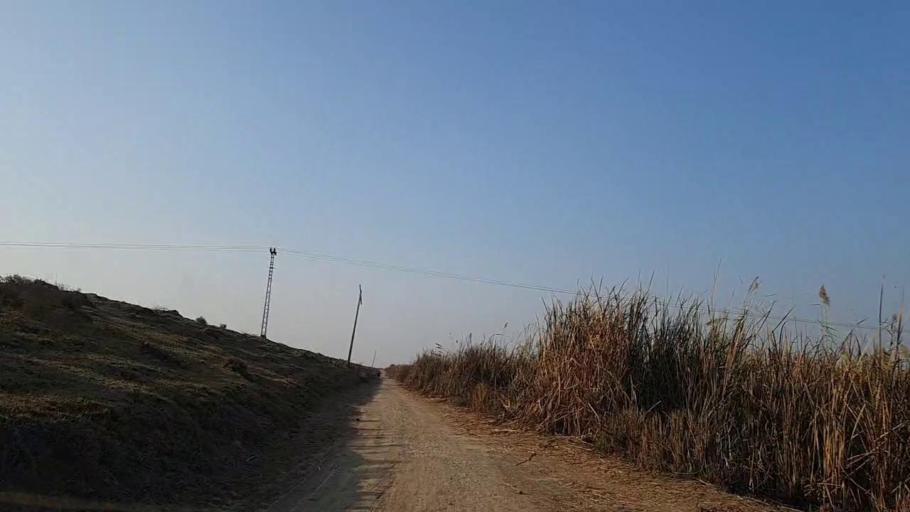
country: PK
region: Sindh
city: Sakrand
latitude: 26.0960
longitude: 68.3713
